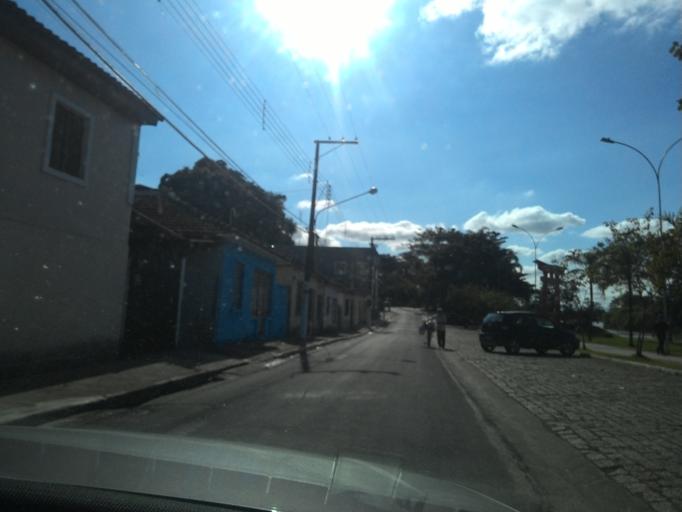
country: BR
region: Sao Paulo
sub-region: Registro
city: Registro
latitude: -24.4903
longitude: -47.8379
